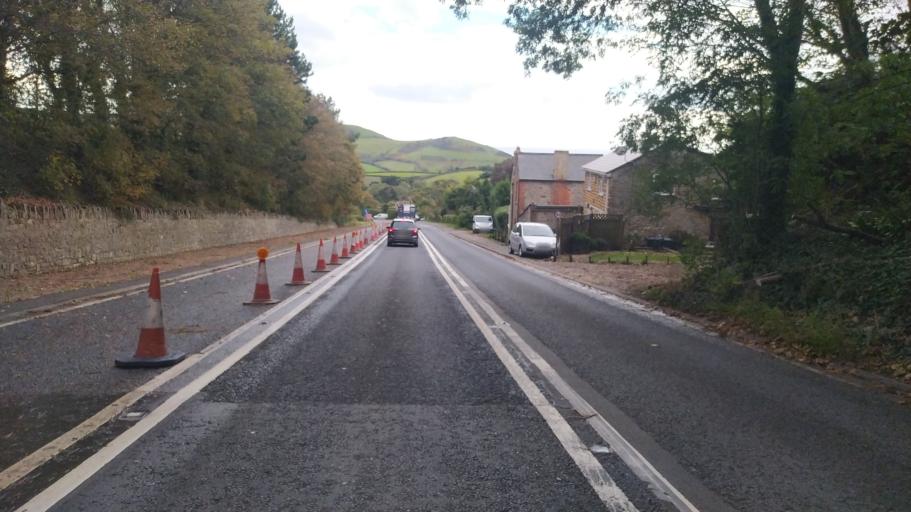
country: GB
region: England
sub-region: Dorset
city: Bridport
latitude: 50.7352
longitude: -2.8286
